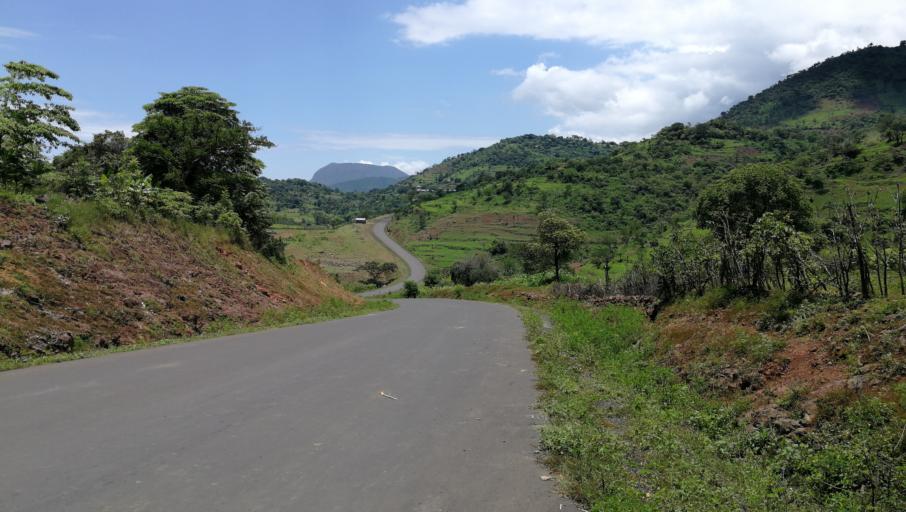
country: ET
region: Southern Nations, Nationalities, and People's Region
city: Areka
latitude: 6.9027
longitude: 37.2919
